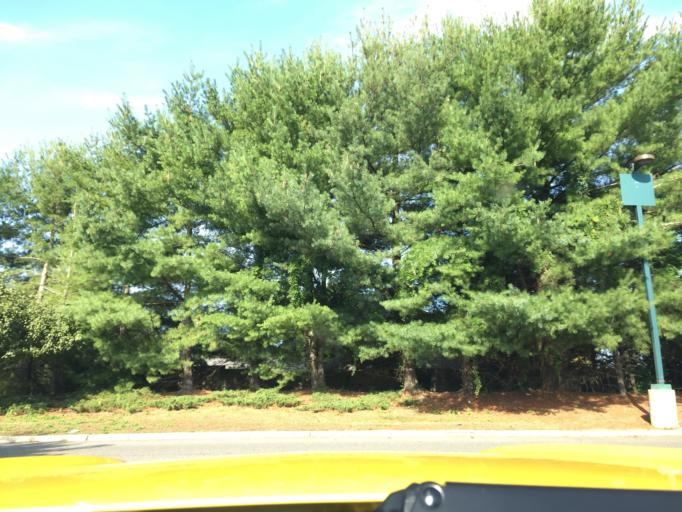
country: US
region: New York
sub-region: Nassau County
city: Hicksville
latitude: 40.7726
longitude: -73.5343
